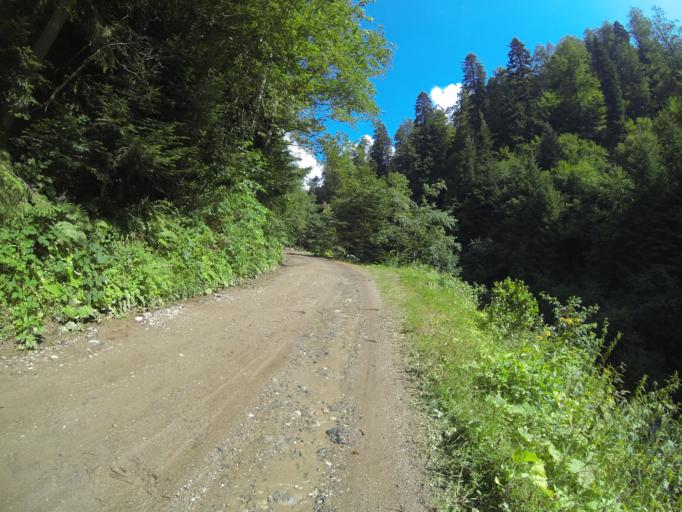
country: RO
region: Valcea
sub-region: Comuna Costesti
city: Bistrita
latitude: 45.2531
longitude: 23.9914
